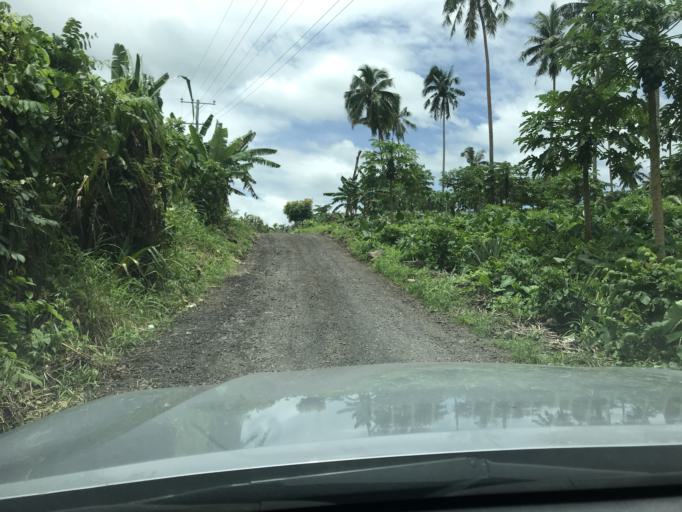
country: WS
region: Tuamasaga
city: Afenga
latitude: -13.8237
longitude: -171.8822
